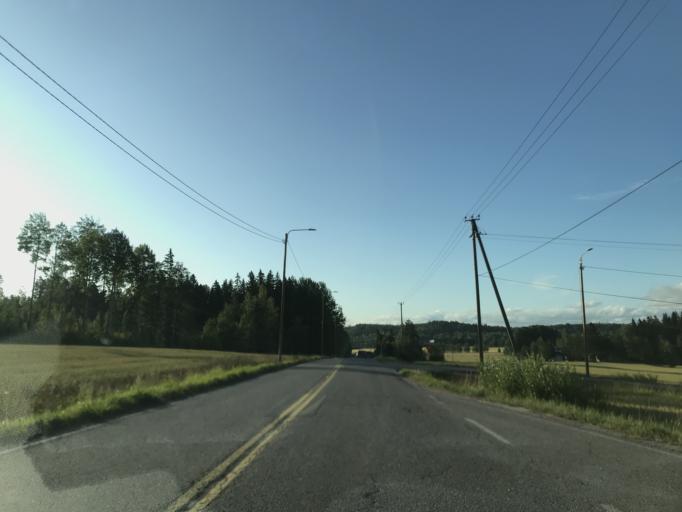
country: FI
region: Uusimaa
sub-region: Helsinki
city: Kauniainen
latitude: 60.3611
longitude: 24.6881
